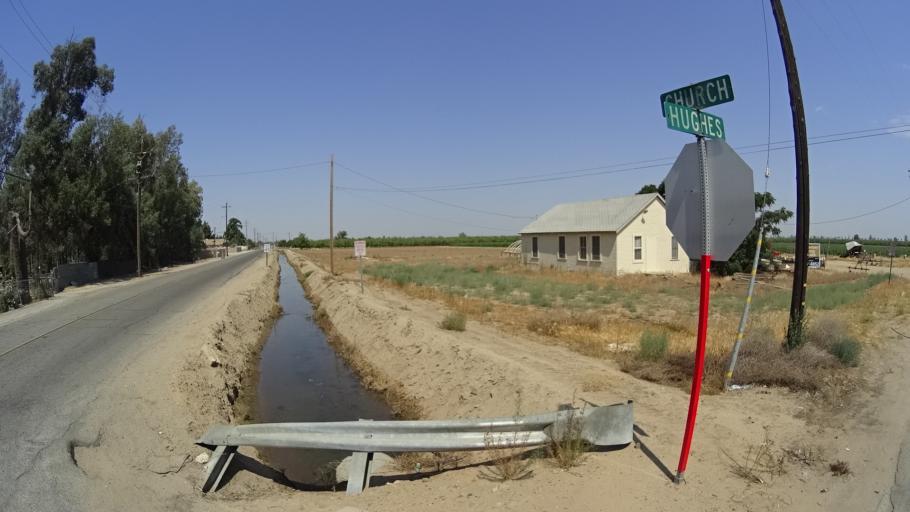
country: US
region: California
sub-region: Fresno County
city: West Park
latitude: 36.7140
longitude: -119.8358
